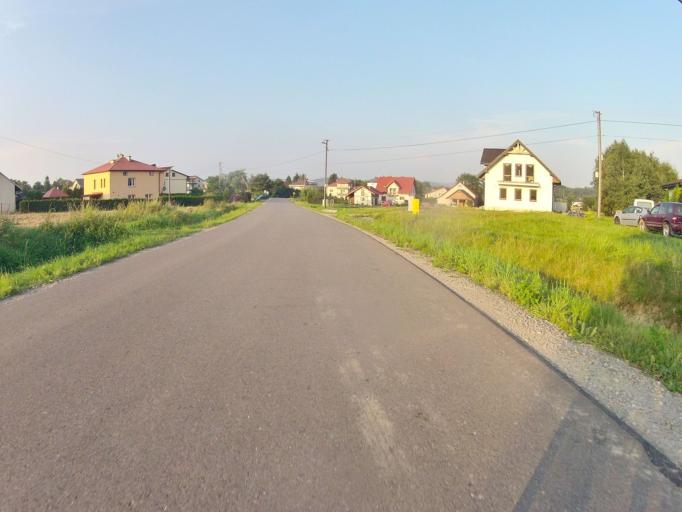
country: PL
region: Subcarpathian Voivodeship
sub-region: Powiat jasielski
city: Brzyska
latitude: 49.7882
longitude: 21.3977
